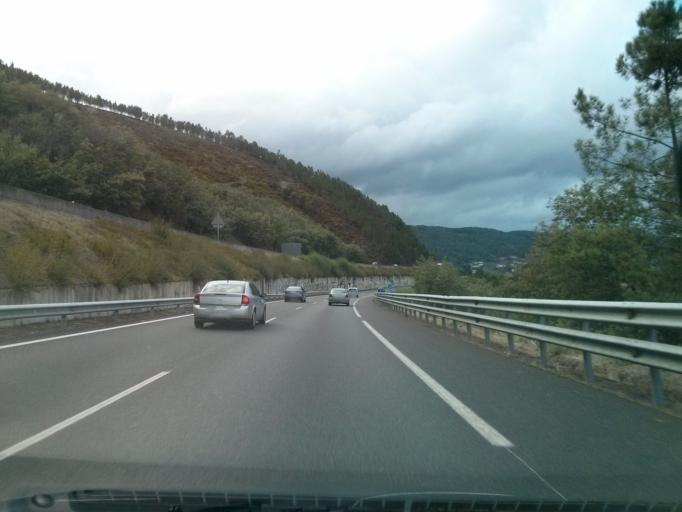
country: ES
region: Galicia
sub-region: Provincia de Ourense
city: Toen
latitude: 42.3354
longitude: -7.9837
